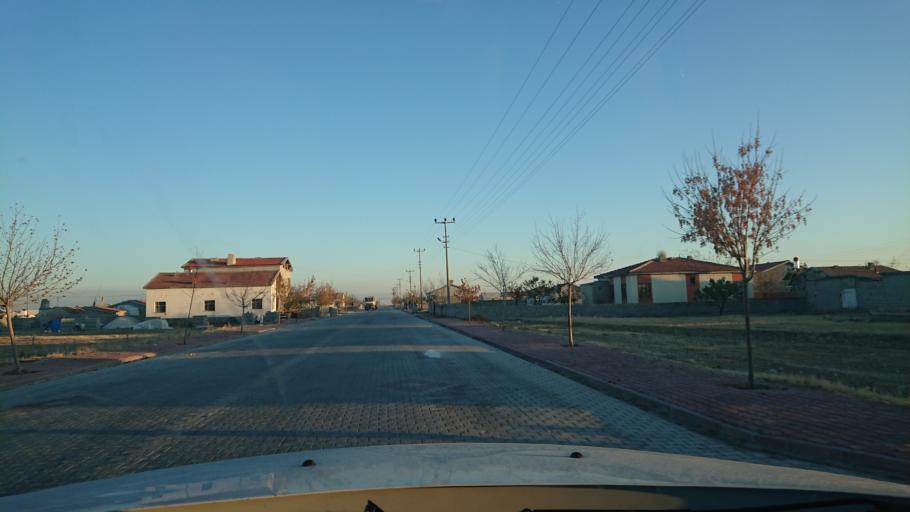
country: TR
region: Aksaray
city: Eskil
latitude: 38.3970
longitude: 33.4218
